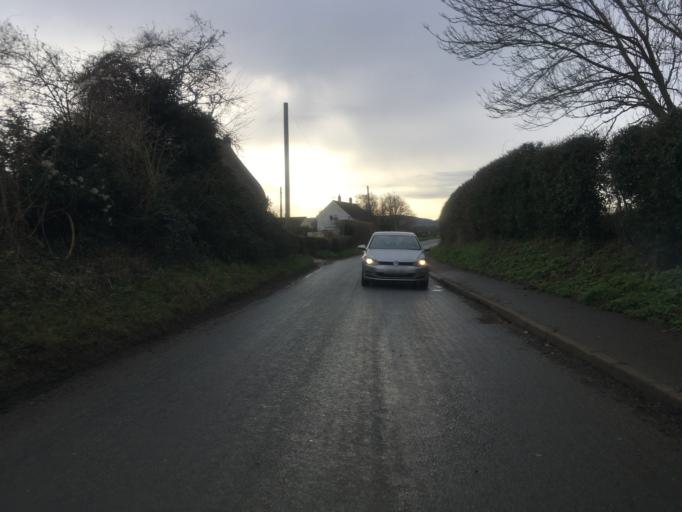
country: GB
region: England
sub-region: Worcestershire
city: Evesham
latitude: 52.0354
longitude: -2.0064
